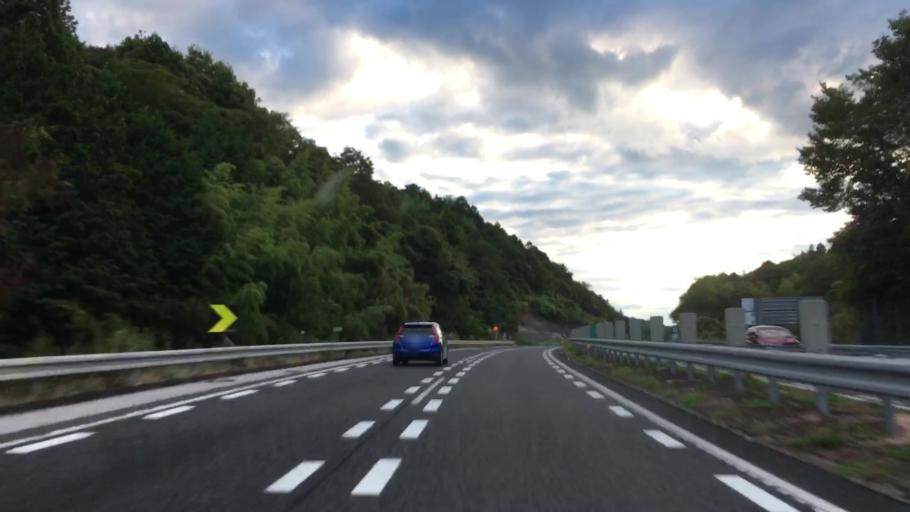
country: JP
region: Yamaguchi
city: Onoda
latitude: 34.1164
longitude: 131.1759
